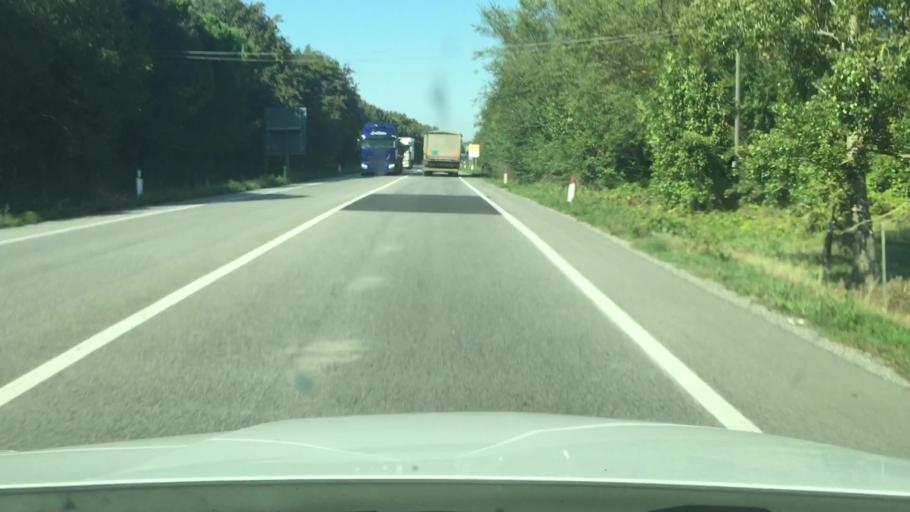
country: IT
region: Emilia-Romagna
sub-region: Provincia di Ravenna
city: Ravenna
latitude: 44.4644
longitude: 12.2090
